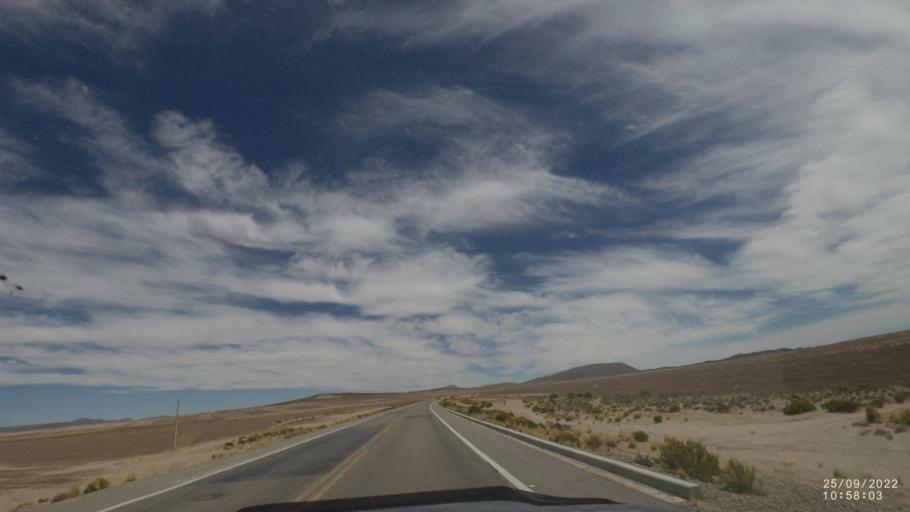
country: BO
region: Oruro
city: Challapata
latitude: -19.4684
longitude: -66.9005
